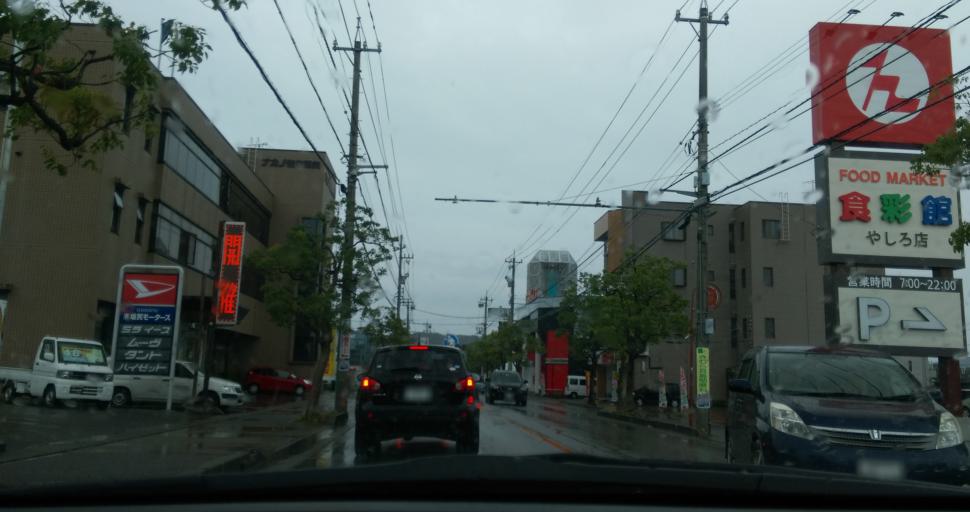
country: JP
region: Fukui
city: Fukui-shi
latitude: 36.0561
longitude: 136.1881
